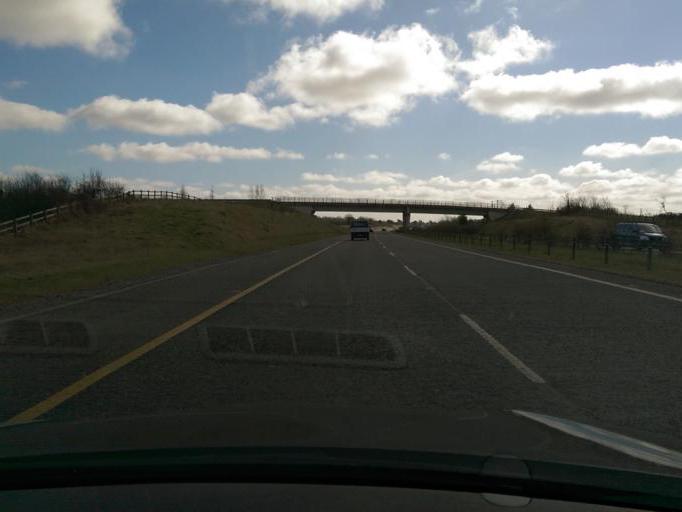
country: IE
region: Leinster
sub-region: An Mhi
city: Longwood
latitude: 53.4359
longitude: -7.0035
